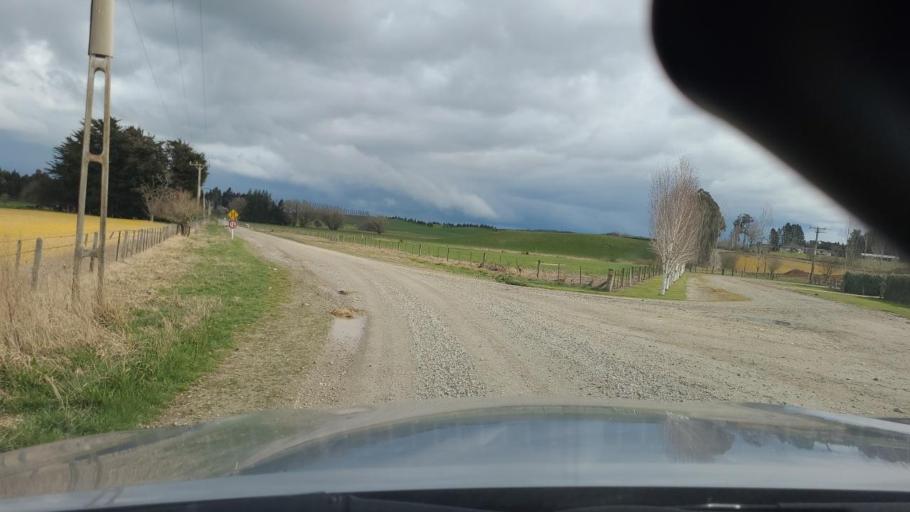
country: NZ
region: Otago
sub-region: Queenstown-Lakes District
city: Kingston
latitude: -45.7265
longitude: 168.7746
